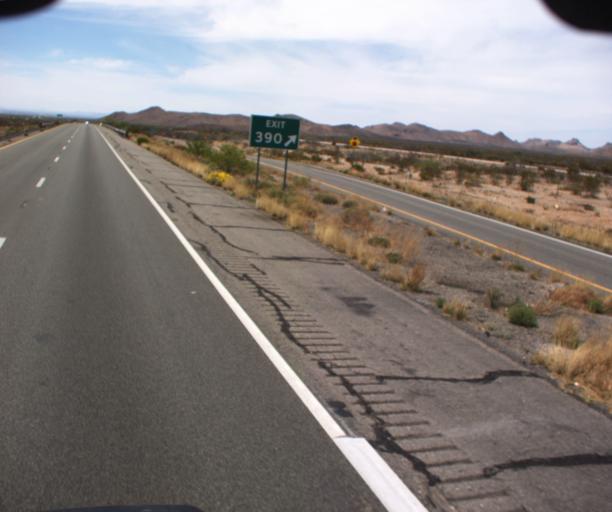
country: US
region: New Mexico
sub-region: Hidalgo County
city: Lordsburg
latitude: 32.2289
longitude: -109.0529
